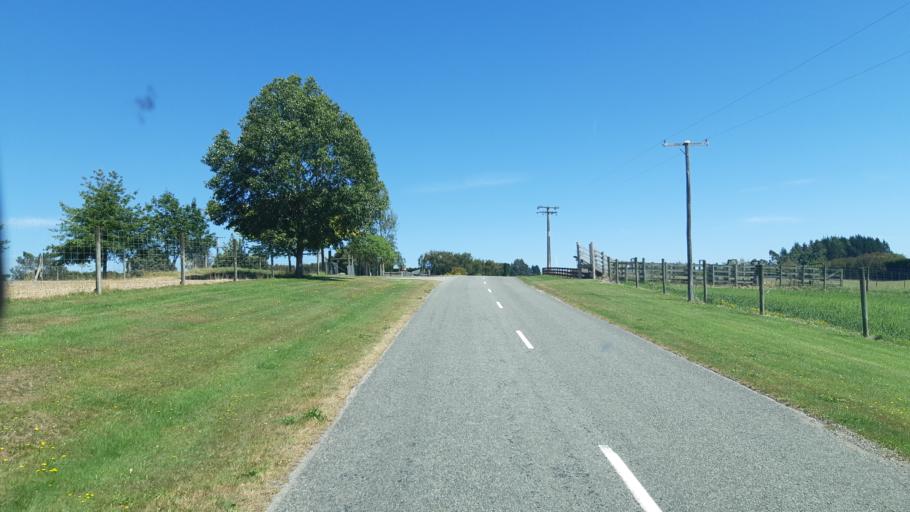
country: NZ
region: Canterbury
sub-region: Timaru District
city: Timaru
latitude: -44.3949
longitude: 171.1494
